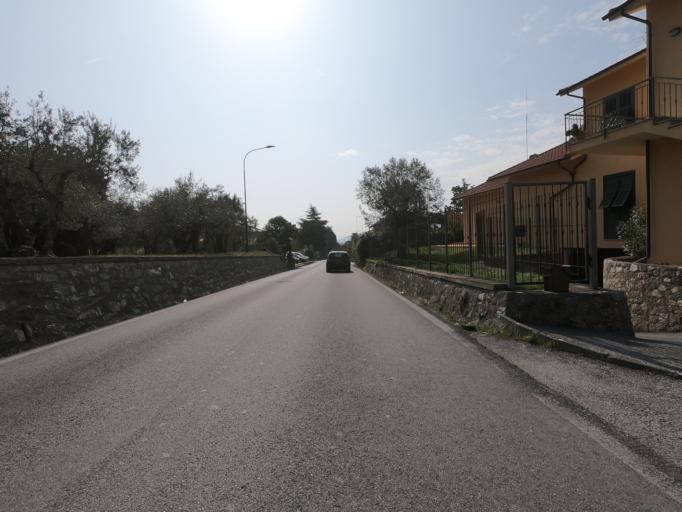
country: IT
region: Liguria
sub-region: Provincia di Savona
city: Cisano
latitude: 44.0870
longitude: 8.1474
